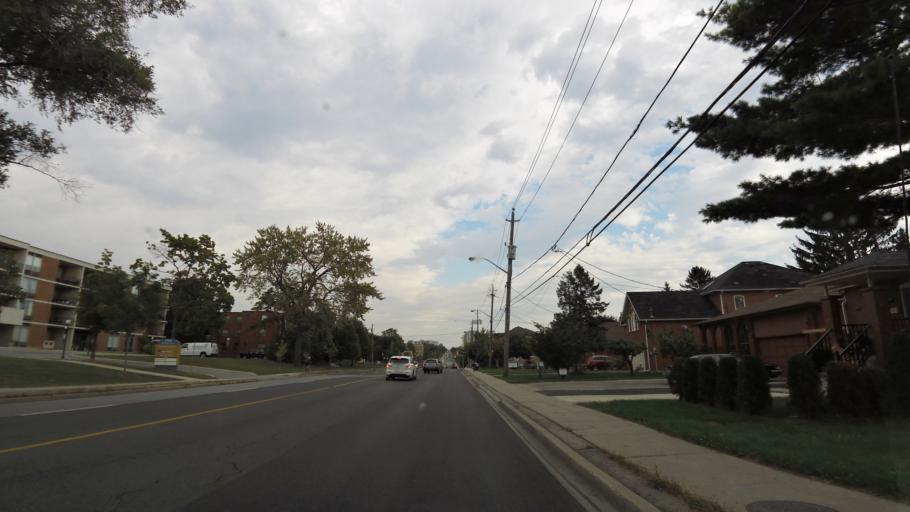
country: CA
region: Ontario
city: Toronto
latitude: 43.7039
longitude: -79.4987
